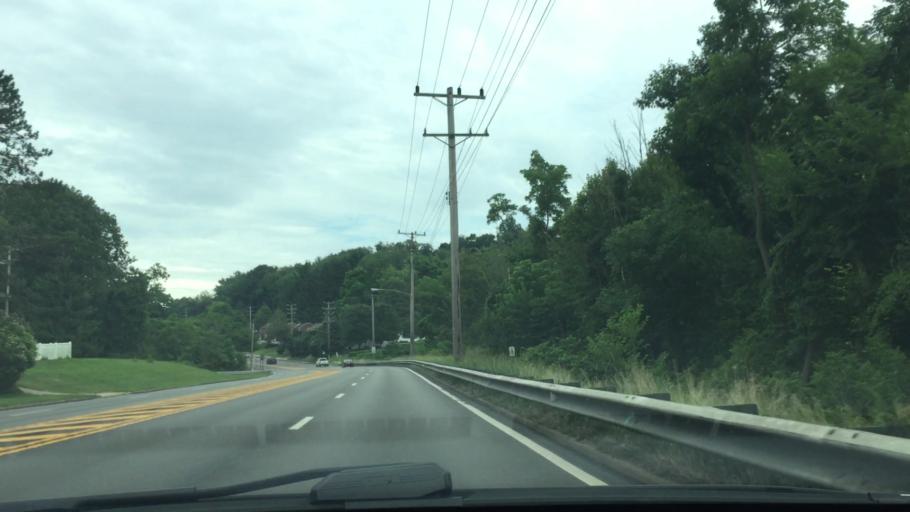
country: US
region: Pennsylvania
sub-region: Allegheny County
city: Mount Lebanon
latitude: 40.3600
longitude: -80.0615
